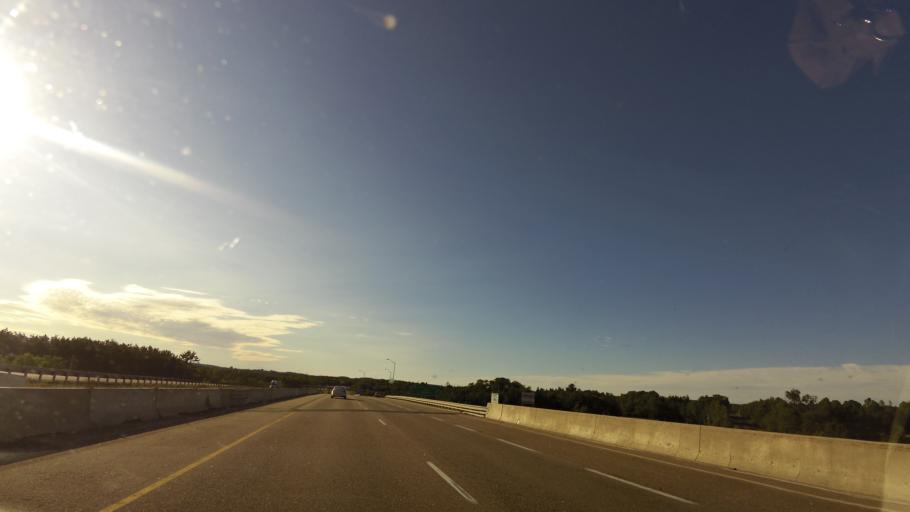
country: CA
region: Ontario
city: Barrie
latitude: 44.5190
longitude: -79.7357
